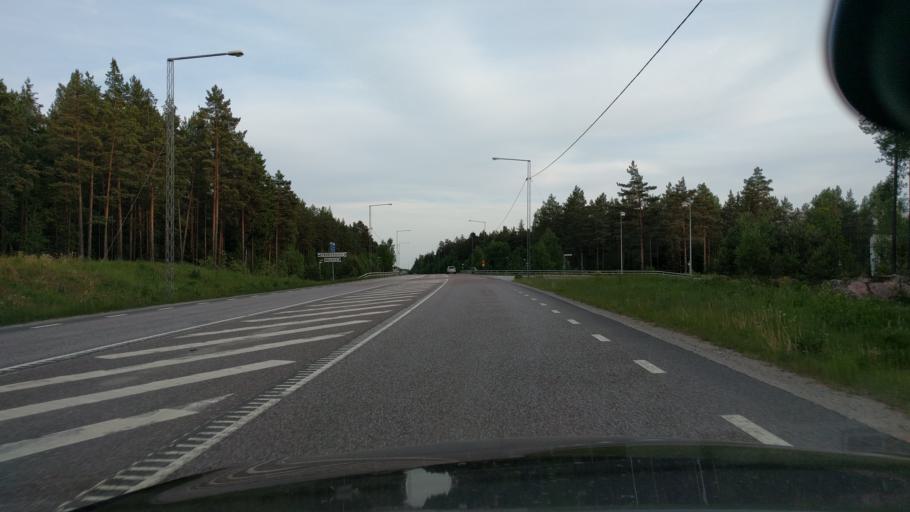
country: SE
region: Stockholm
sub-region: Vallentuna Kommun
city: Vallentuna
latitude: 59.5143
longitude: 18.0946
